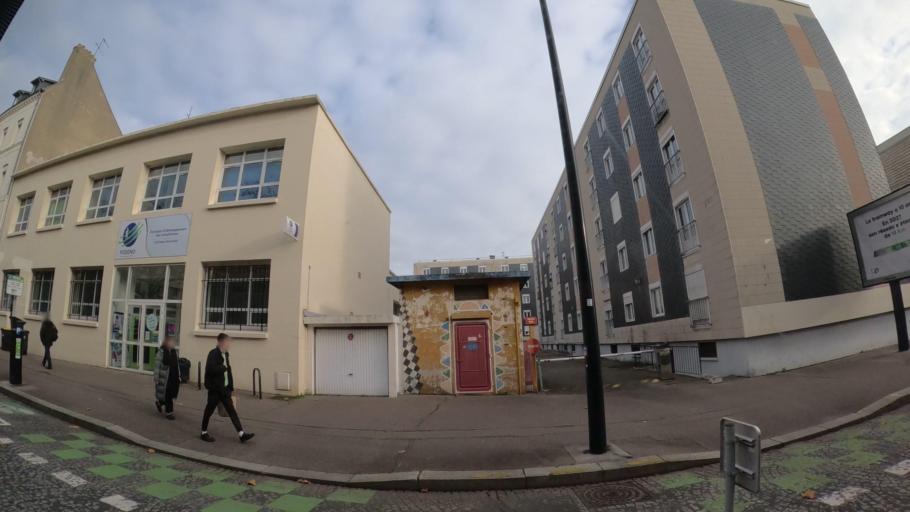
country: FR
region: Haute-Normandie
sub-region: Departement de la Seine-Maritime
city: Le Havre
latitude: 49.4916
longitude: 0.1169
